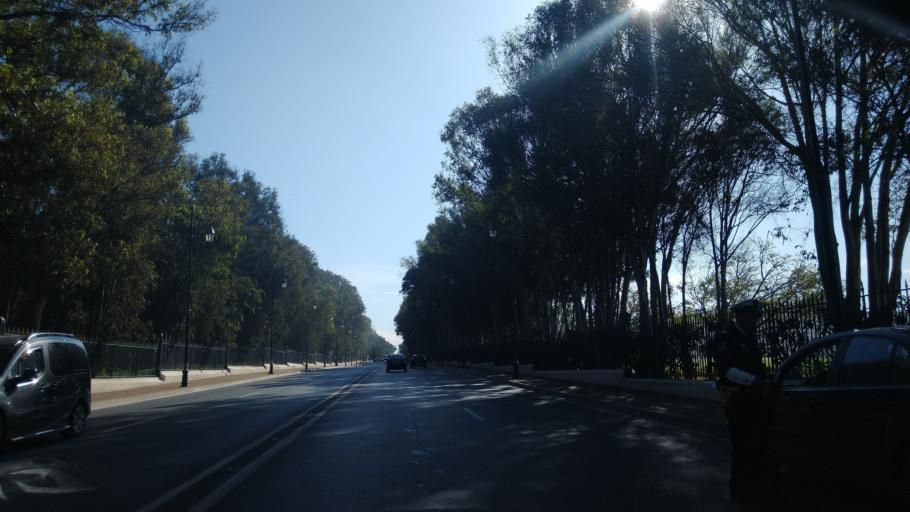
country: MA
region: Rabat-Sale-Zemmour-Zaer
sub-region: Rabat
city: Rabat
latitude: 33.9840
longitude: -6.8480
